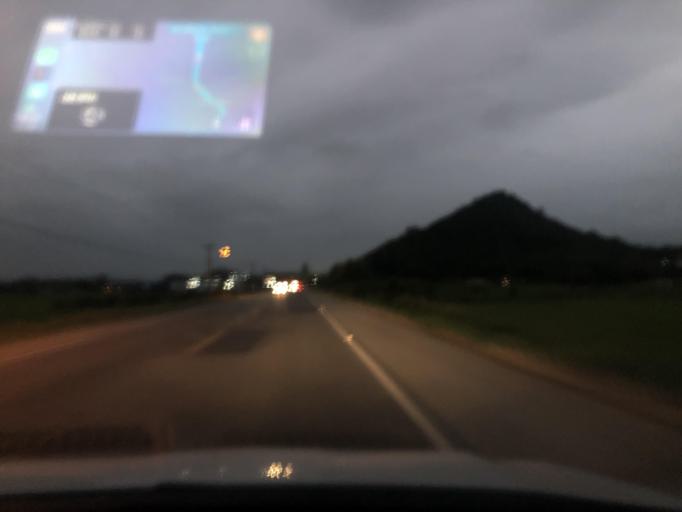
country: BR
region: Santa Catarina
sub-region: Guaramirim
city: Guaramirim
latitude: -26.6073
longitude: -49.0080
